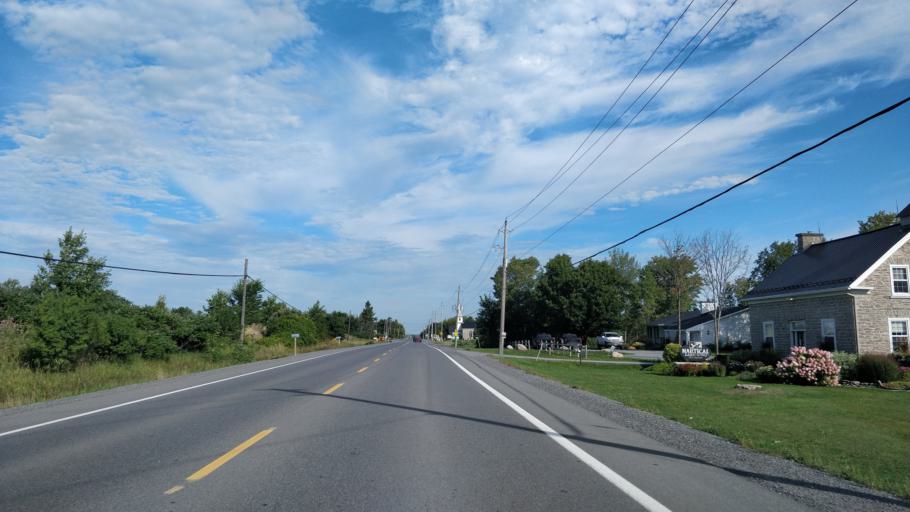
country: CA
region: Ontario
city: Bells Corners
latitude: 45.3116
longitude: -75.9949
